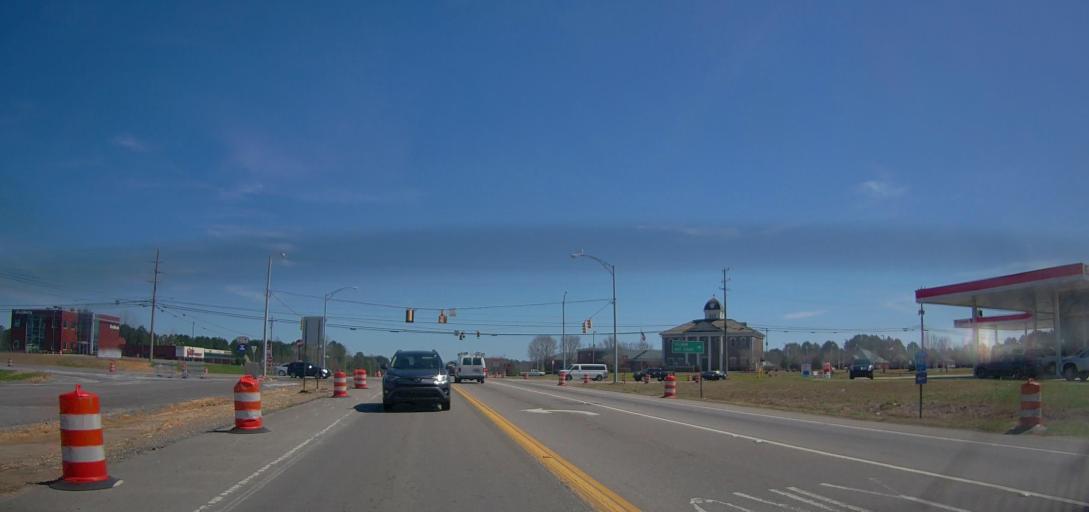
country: US
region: Alabama
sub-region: Cullman County
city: Cullman
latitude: 34.2033
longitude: -86.8285
